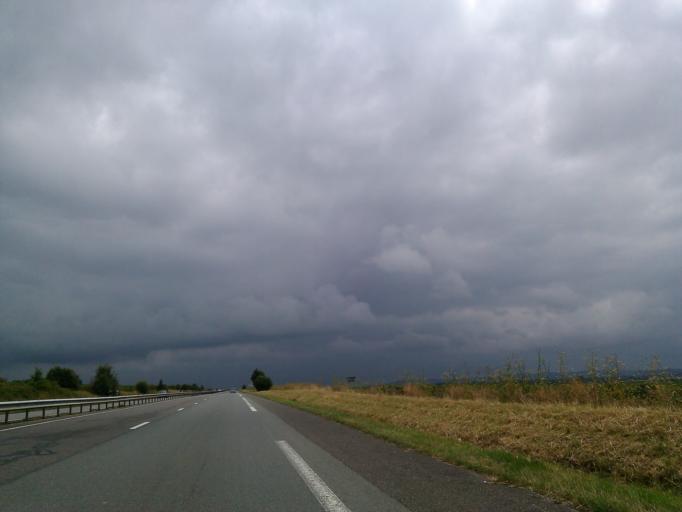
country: FR
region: Poitou-Charentes
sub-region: Departement de la Charente
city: Gensac-la-Pallue
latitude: 45.6691
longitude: -0.2510
